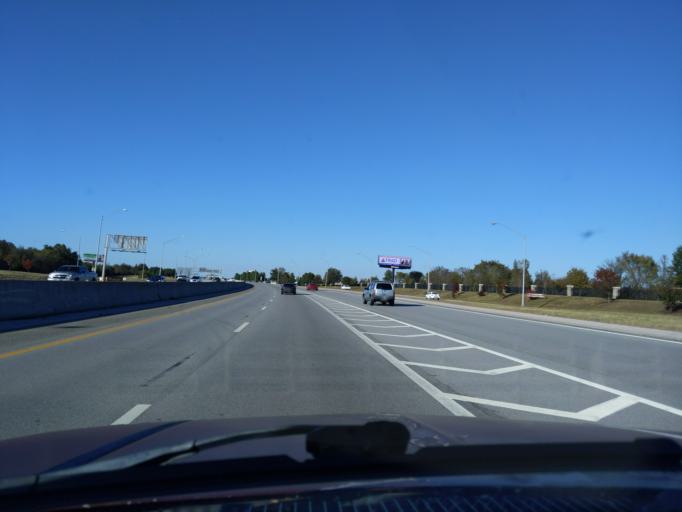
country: US
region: Oklahoma
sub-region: Tulsa County
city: Broken Arrow
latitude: 36.0351
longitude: -95.8592
